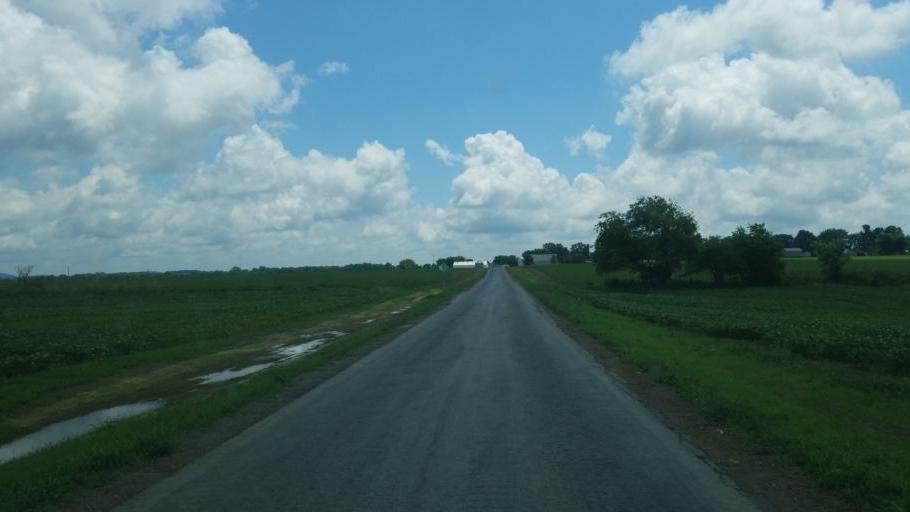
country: US
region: Ohio
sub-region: Highland County
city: Greenfield
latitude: 39.2660
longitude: -83.4504
